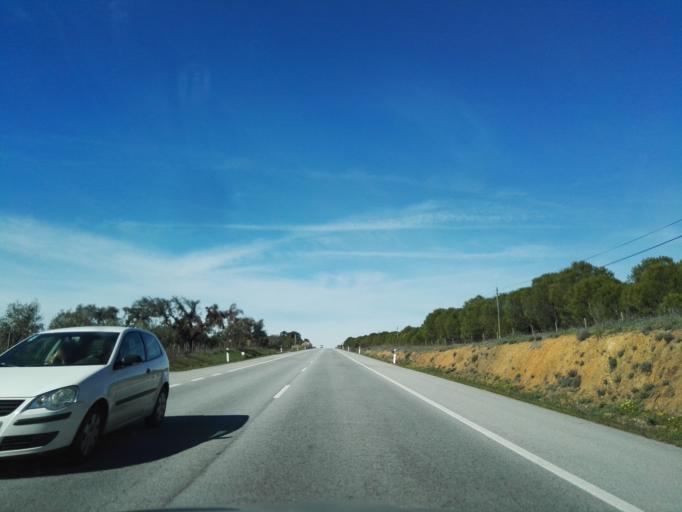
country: PT
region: Portalegre
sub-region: Arronches
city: Arronches
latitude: 39.1455
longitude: -7.3042
